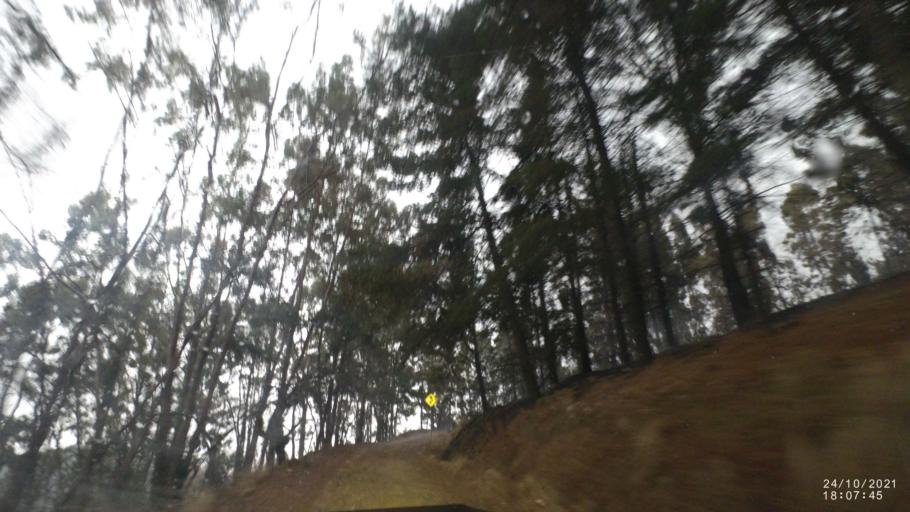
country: BO
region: Cochabamba
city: Cochabamba
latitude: -17.3284
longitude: -66.1350
